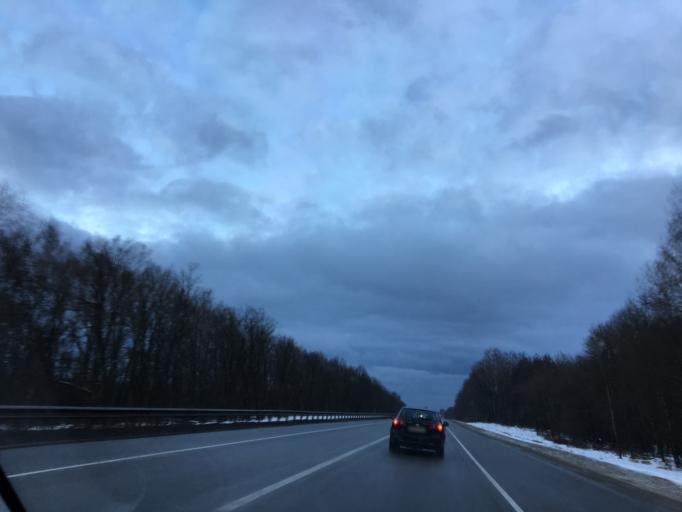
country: RU
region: Tula
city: Leninskiy
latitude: 54.3669
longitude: 37.5265
